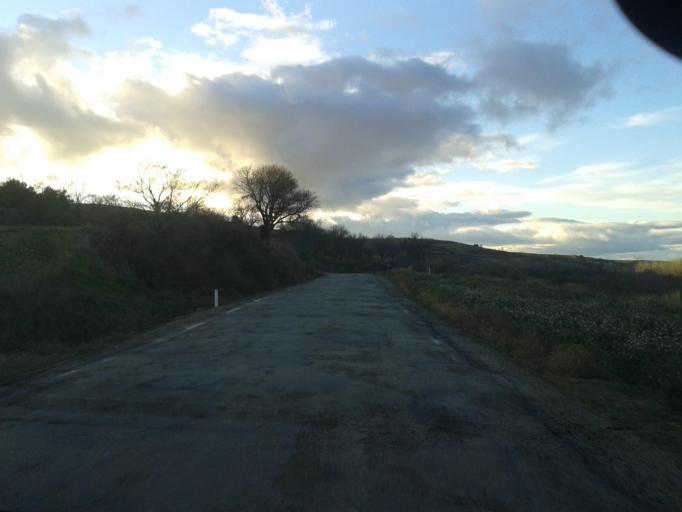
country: ES
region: Aragon
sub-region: Provincia de Teruel
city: Lagueruela
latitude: 41.0400
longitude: -1.2000
